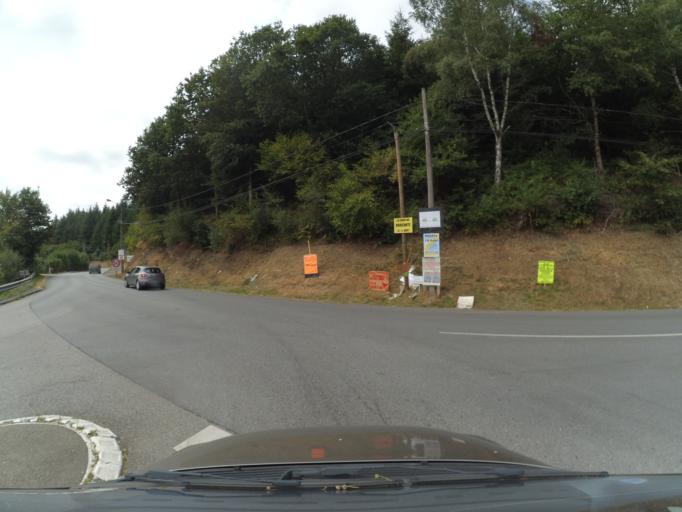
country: FR
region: Limousin
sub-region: Departement de la Correze
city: Ussel
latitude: 45.5424
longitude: 2.2979
